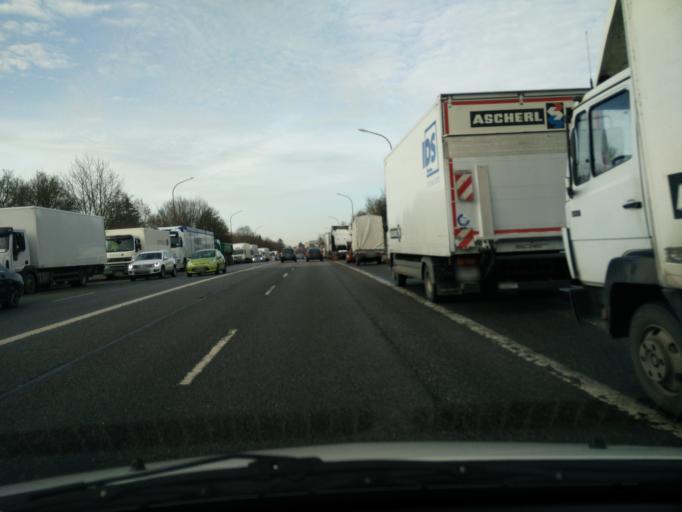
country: DE
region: Bavaria
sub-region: Upper Bavaria
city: Karlsfeld
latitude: 48.1750
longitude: 11.5011
